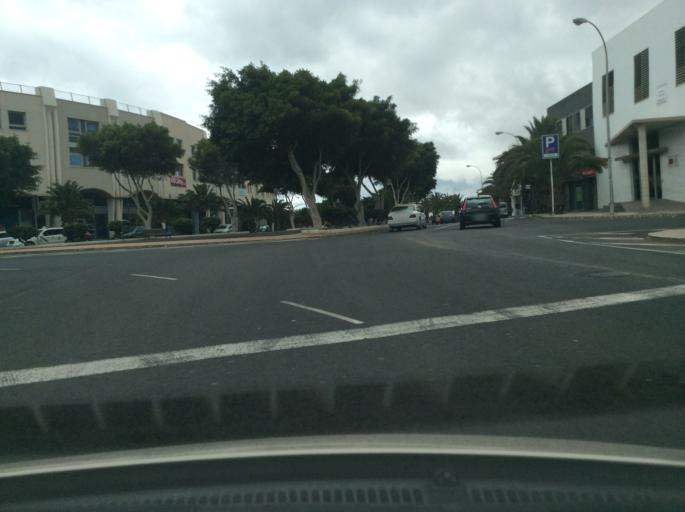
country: ES
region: Canary Islands
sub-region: Provincia de Las Palmas
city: Arrecife
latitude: 28.9660
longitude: -13.5577
